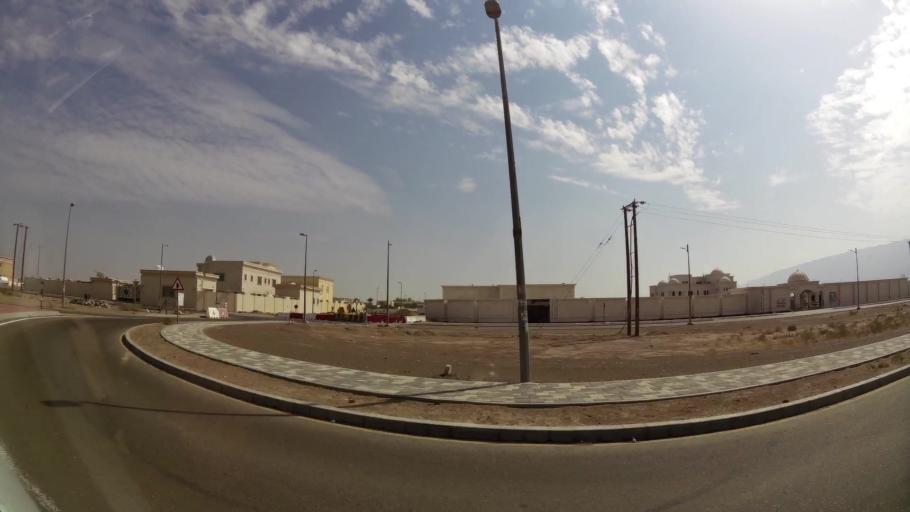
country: AE
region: Abu Dhabi
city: Al Ain
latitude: 24.0889
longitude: 55.8469
